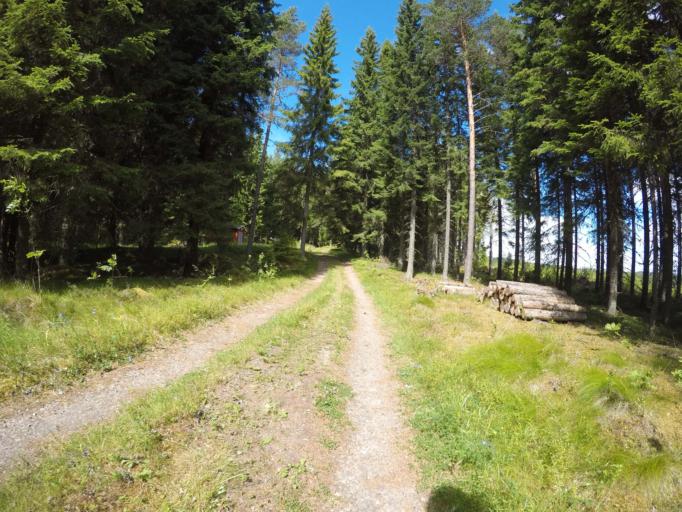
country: SE
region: Vaermland
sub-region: Filipstads Kommun
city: Lesjofors
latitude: 60.0789
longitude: 14.4572
